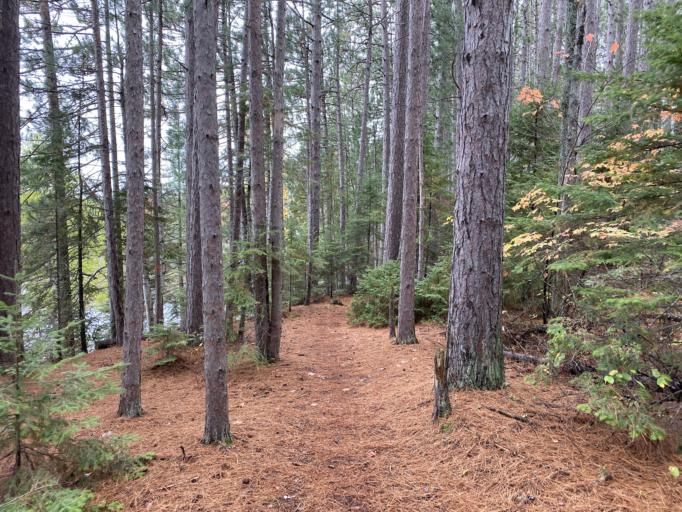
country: US
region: Michigan
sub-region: Marquette County
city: West Ishpeming
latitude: 46.5331
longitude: -88.0020
